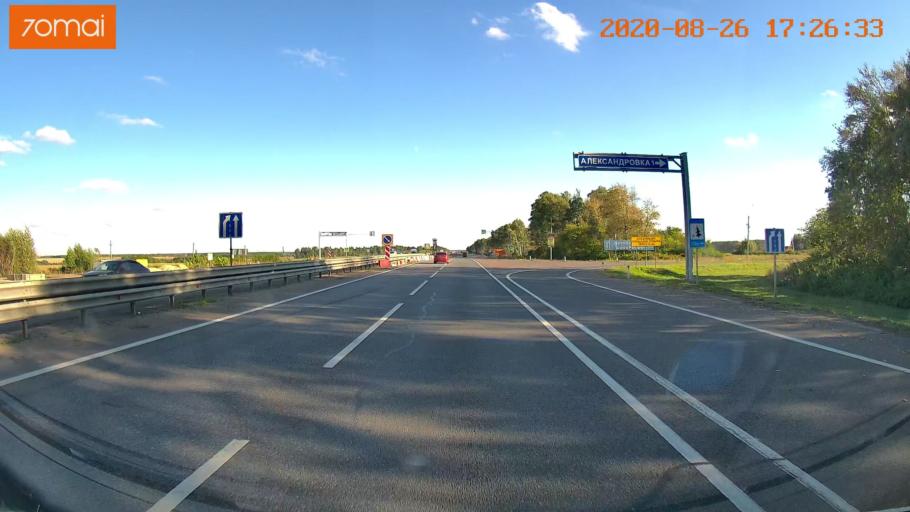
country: RU
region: Tula
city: Kazachka
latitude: 53.4852
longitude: 38.1179
